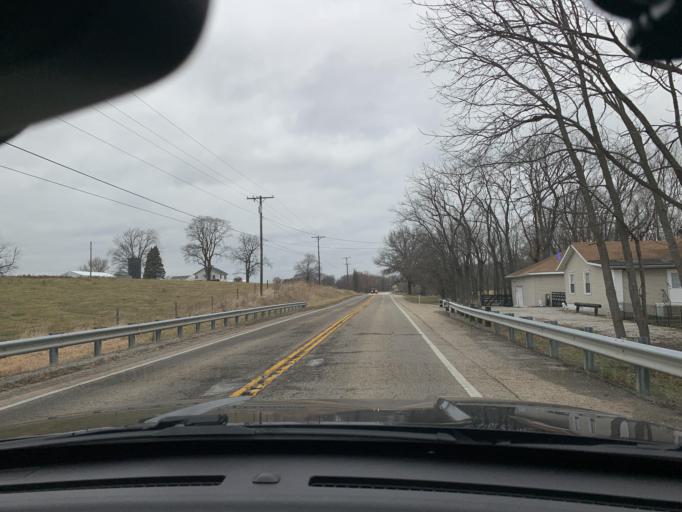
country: US
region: Illinois
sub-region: Sangamon County
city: Jerome
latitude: 39.7264
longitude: -89.6910
